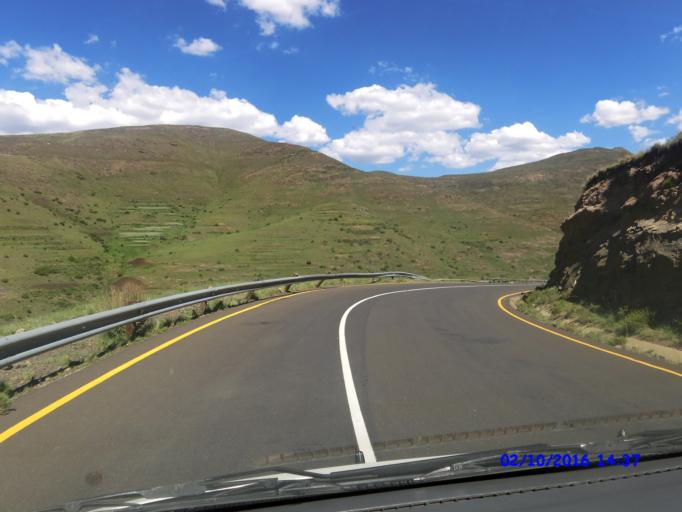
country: LS
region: Maseru
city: Nako
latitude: -29.5007
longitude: 28.0620
